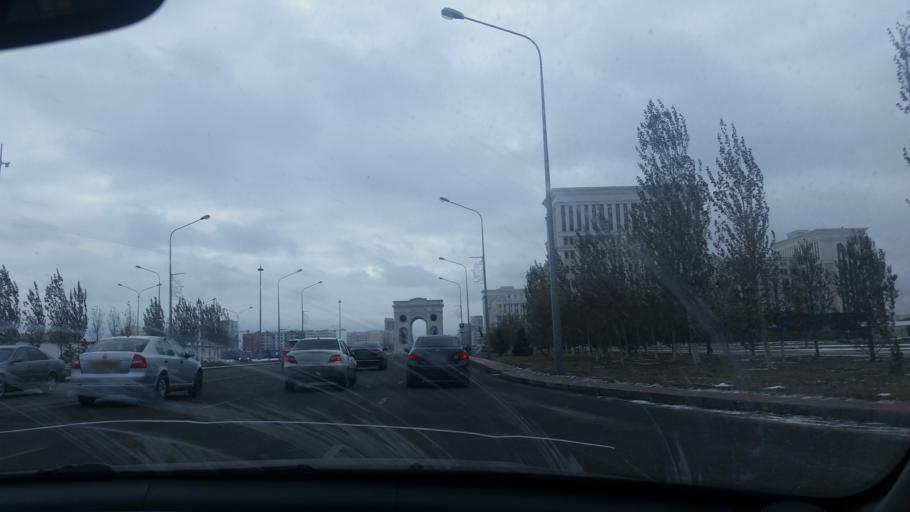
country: KZ
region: Astana Qalasy
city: Astana
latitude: 51.1072
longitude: 71.4309
